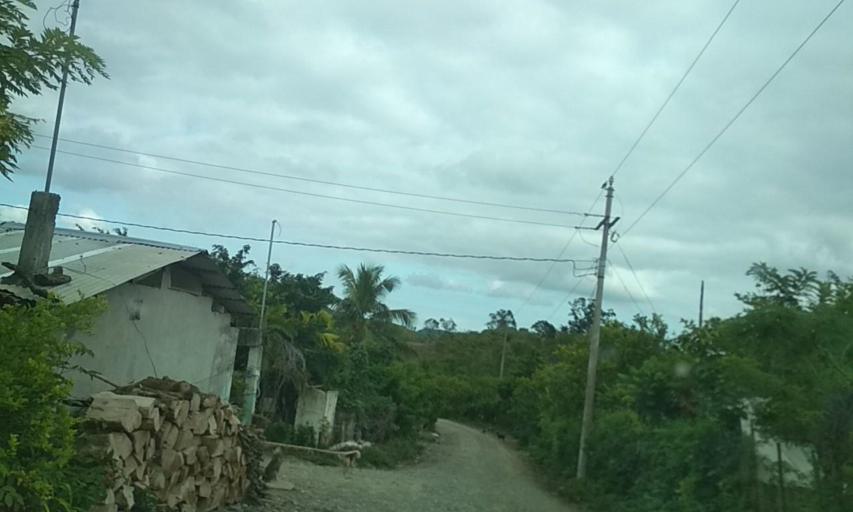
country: MX
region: Veracruz
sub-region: Papantla
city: Polutla
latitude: 20.5808
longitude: -97.2741
